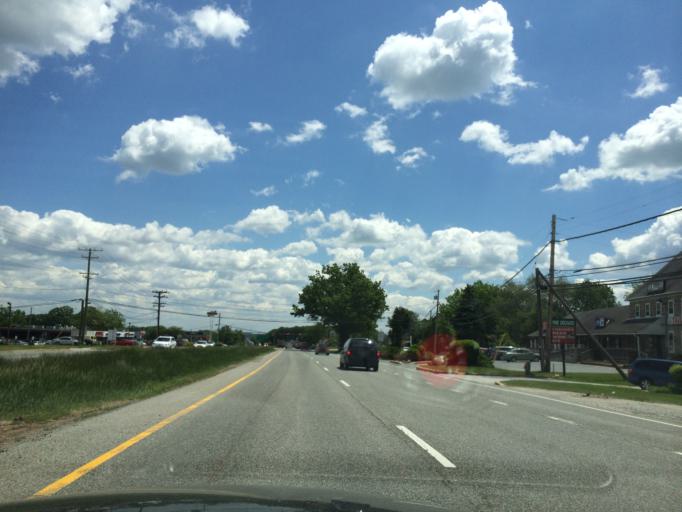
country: US
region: Maryland
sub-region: Howard County
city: Columbia
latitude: 39.2802
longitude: -76.8679
